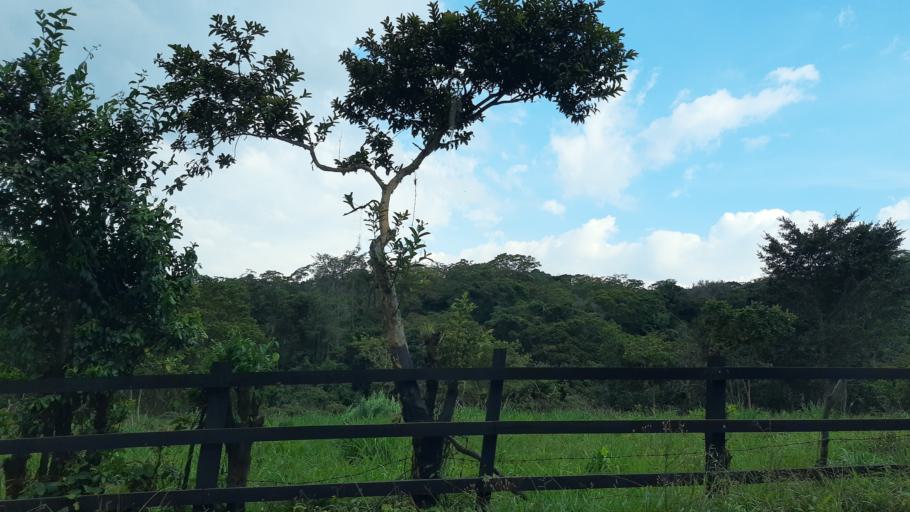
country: CO
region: Boyaca
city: Moniquira
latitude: 5.8107
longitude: -73.6005
